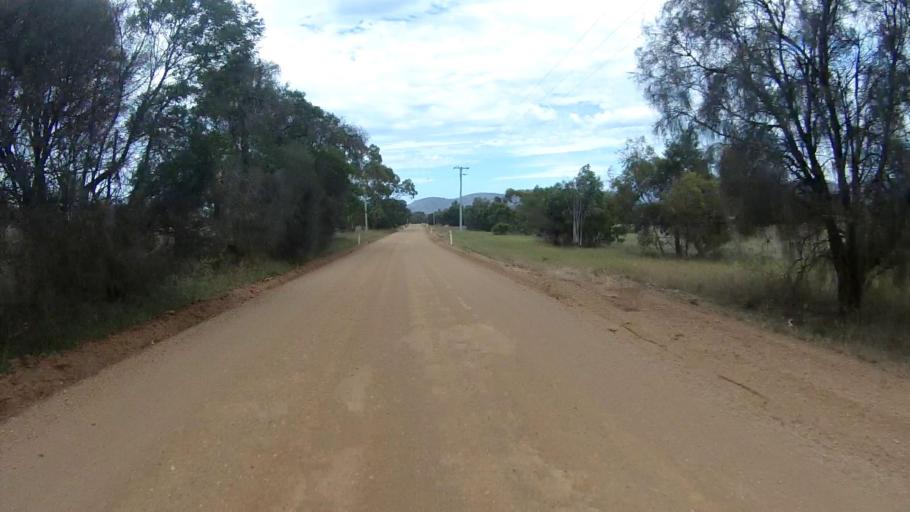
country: AU
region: Tasmania
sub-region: Clarence
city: Cambridge
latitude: -42.7065
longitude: 147.4566
